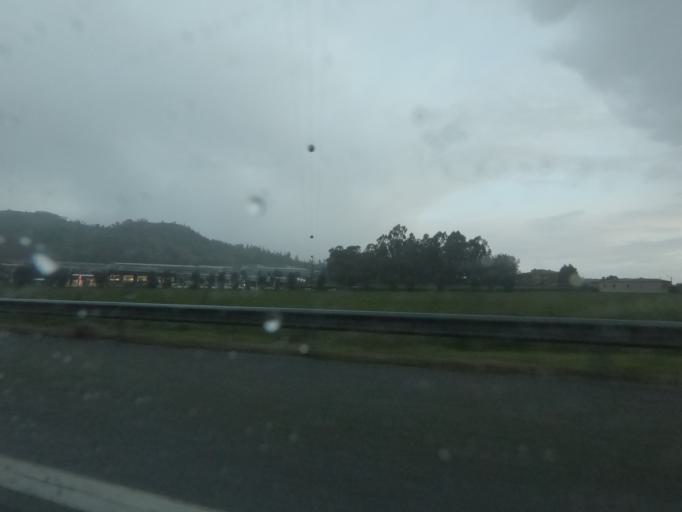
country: PT
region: Braga
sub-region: Braga
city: Braga
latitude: 41.5327
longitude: -8.4590
